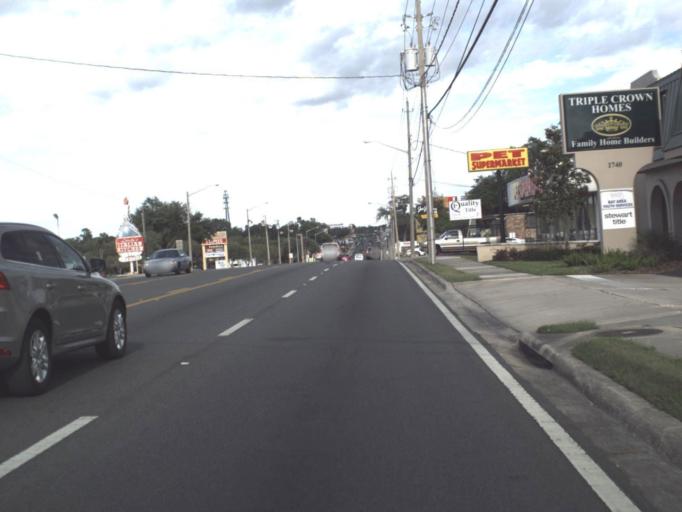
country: US
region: Florida
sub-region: Marion County
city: Ocala
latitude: 29.1869
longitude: -82.1144
